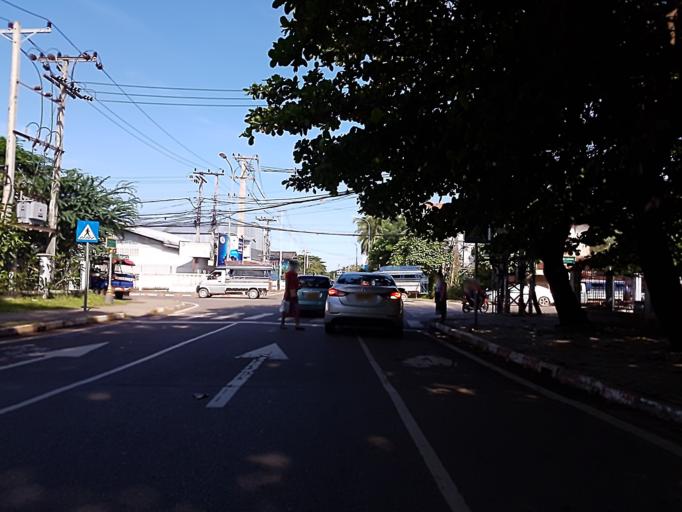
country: LA
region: Vientiane
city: Vientiane
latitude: 17.9627
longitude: 102.6142
